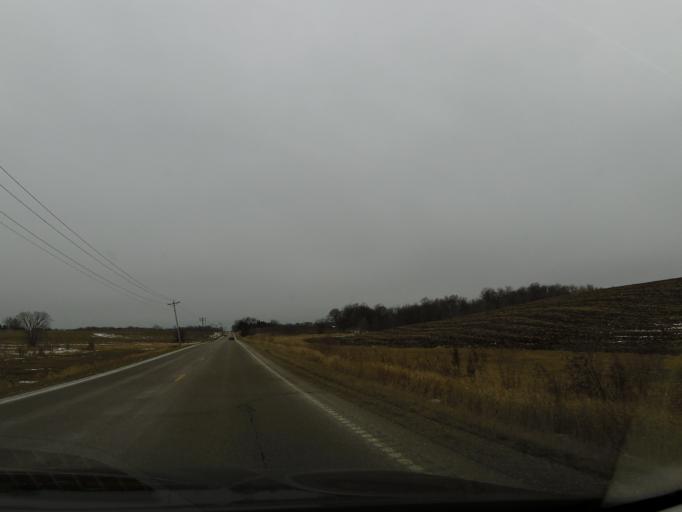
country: US
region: Minnesota
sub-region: Carver County
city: Cologne
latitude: 44.7991
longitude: -93.7882
